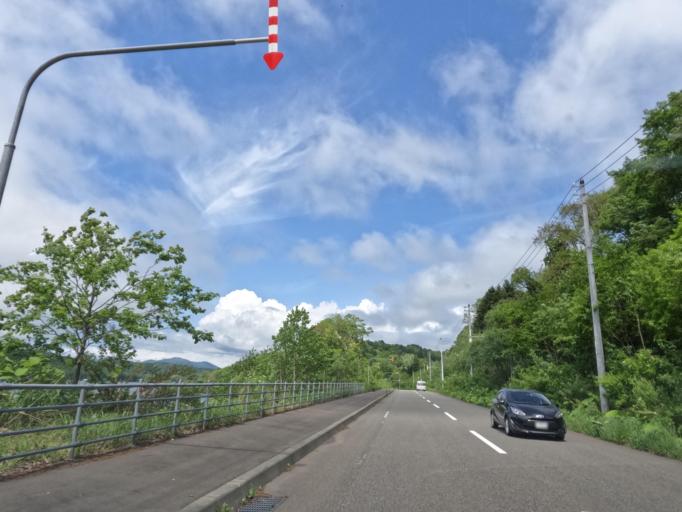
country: JP
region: Hokkaido
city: Tobetsu
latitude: 43.3516
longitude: 141.5684
